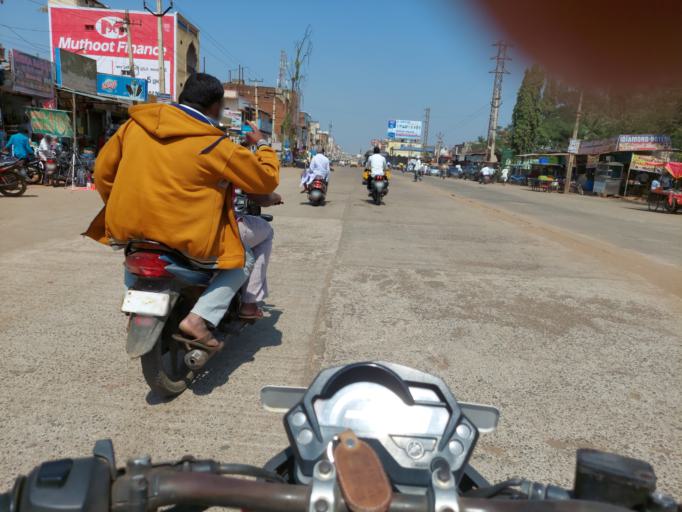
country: IN
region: Telangana
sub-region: Rangareddi
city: Vikarabad
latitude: 17.3402
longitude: 77.9050
